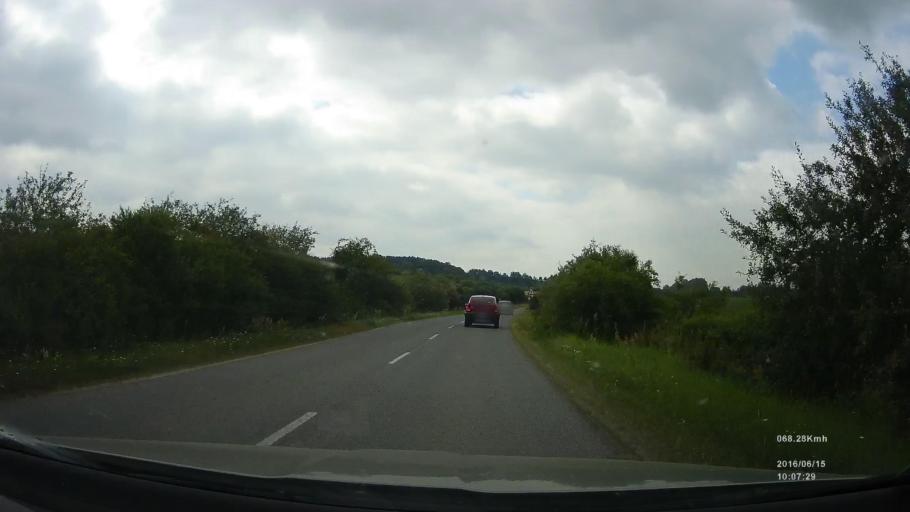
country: SK
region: Kosicky
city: Kosice
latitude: 48.7768
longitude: 21.3297
